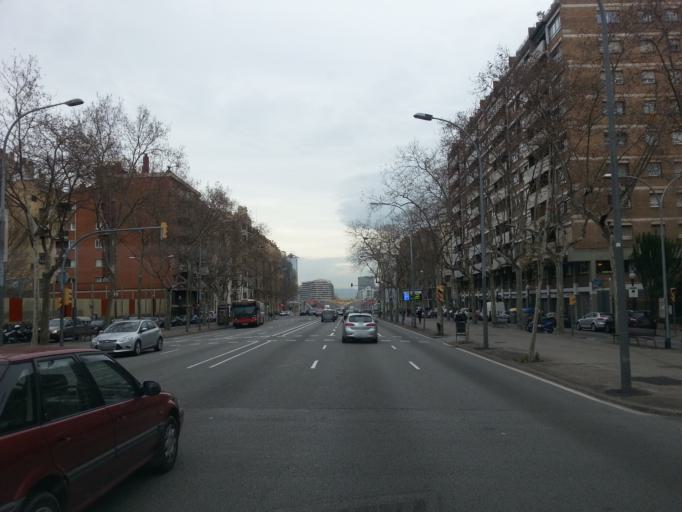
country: ES
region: Catalonia
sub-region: Provincia de Barcelona
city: Ciutat Vella
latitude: 41.4000
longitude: 2.1824
